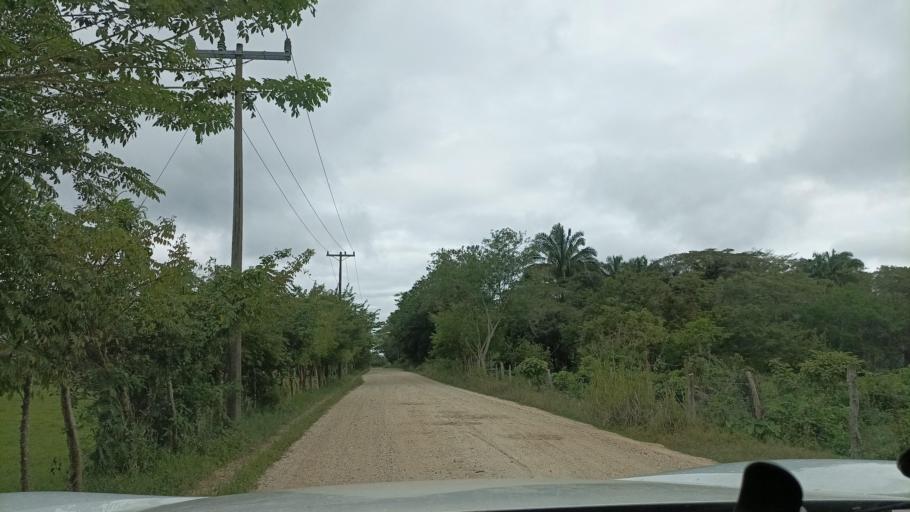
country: MX
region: Veracruz
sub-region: Moloacan
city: Cuichapa
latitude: 17.8430
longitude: -94.3595
